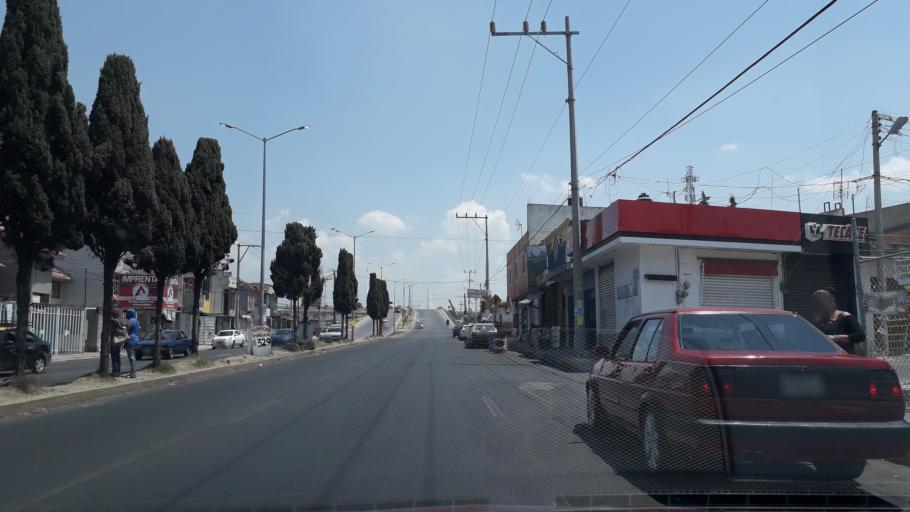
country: MX
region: Puebla
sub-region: Amozoc
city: Casa Blanca
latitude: 19.0656
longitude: -98.1211
